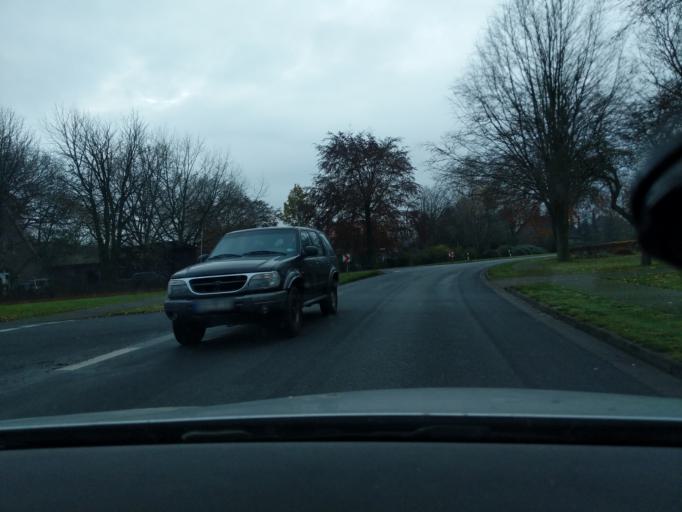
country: DE
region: Lower Saxony
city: Heeslingen
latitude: 53.3352
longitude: 9.3726
